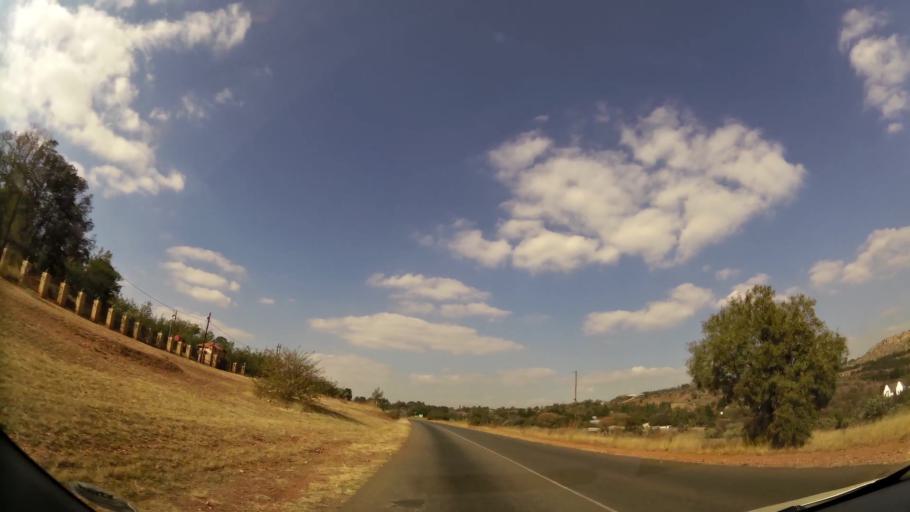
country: ZA
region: Gauteng
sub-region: West Rand District Municipality
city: Krugersdorp
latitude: -26.0442
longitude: 27.7464
